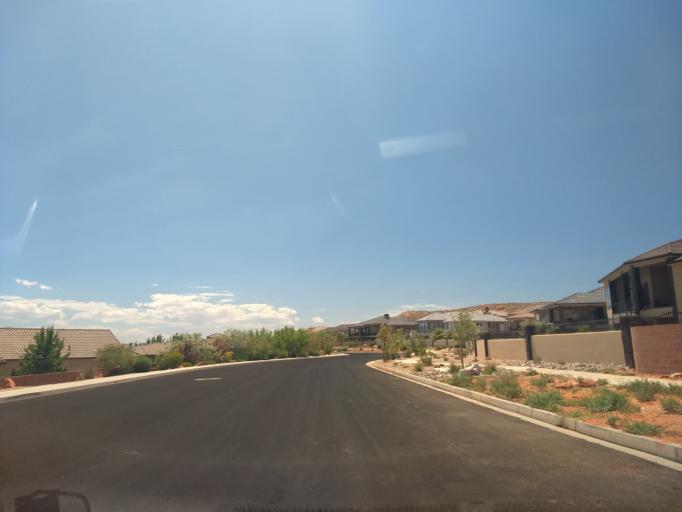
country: US
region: Utah
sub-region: Washington County
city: Washington
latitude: 37.1540
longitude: -113.5310
